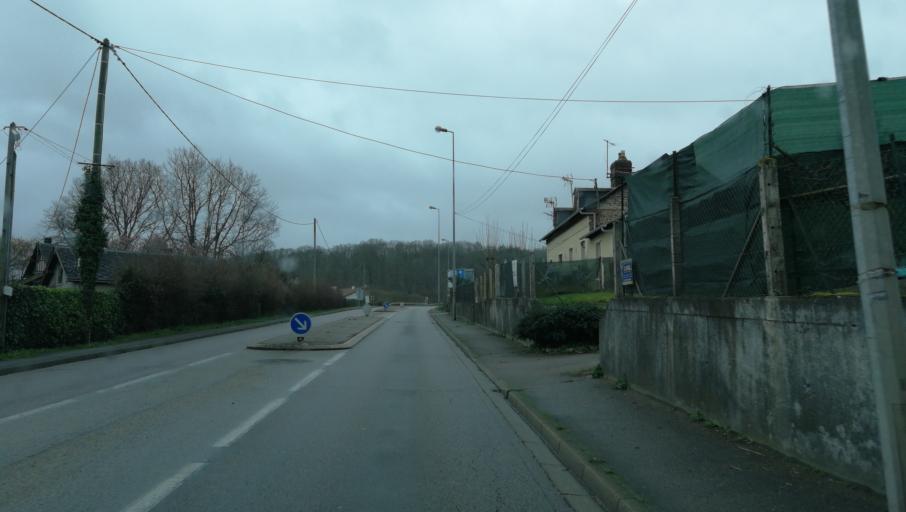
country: FR
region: Haute-Normandie
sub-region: Departement de l'Eure
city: Brionne
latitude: 49.1888
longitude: 0.7100
